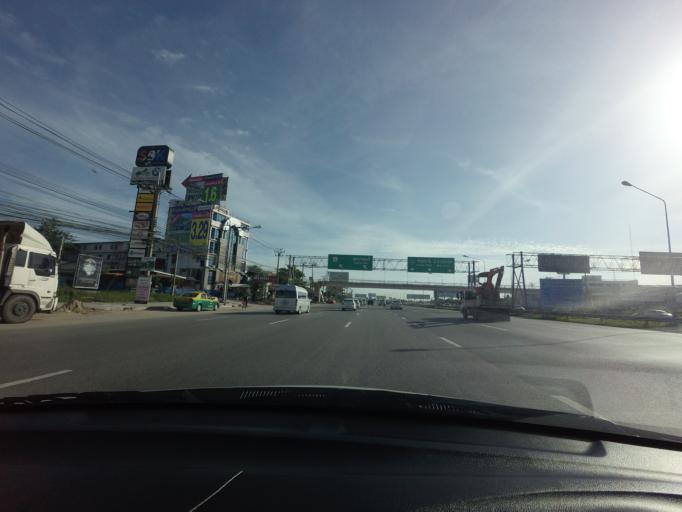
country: TH
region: Nonthaburi
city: Bang Bua Thong
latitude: 13.9320
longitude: 100.4151
